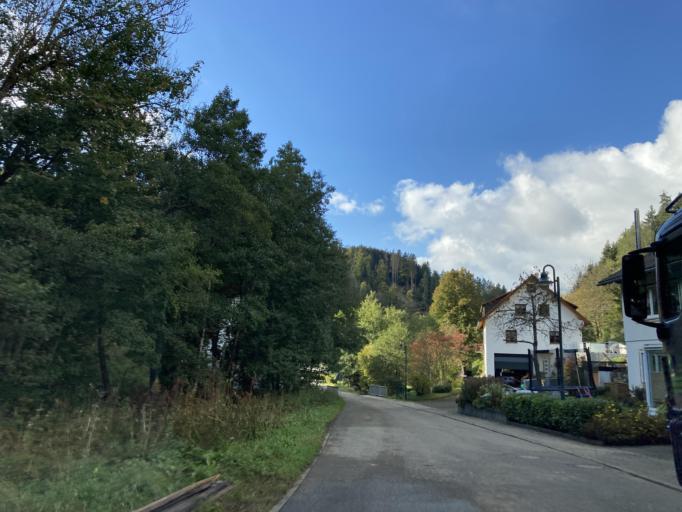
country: DE
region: Baden-Wuerttemberg
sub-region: Freiburg Region
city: Triberg im Schwarzwald
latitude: 48.1253
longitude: 8.2624
